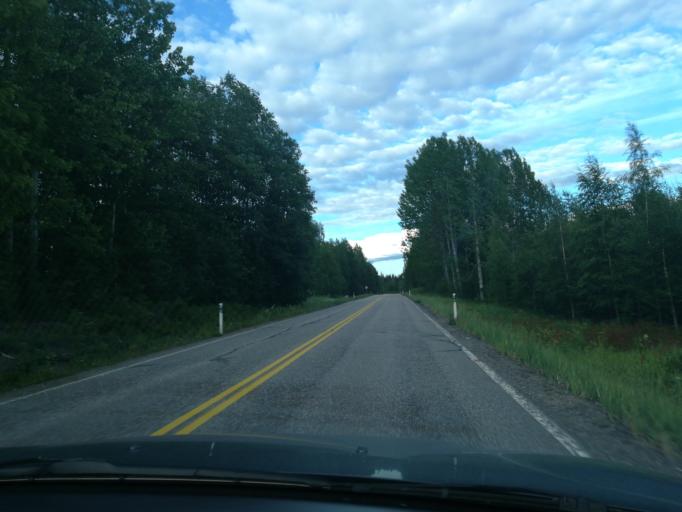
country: FI
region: Southern Savonia
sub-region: Mikkeli
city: Puumala
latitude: 61.5231
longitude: 27.9228
